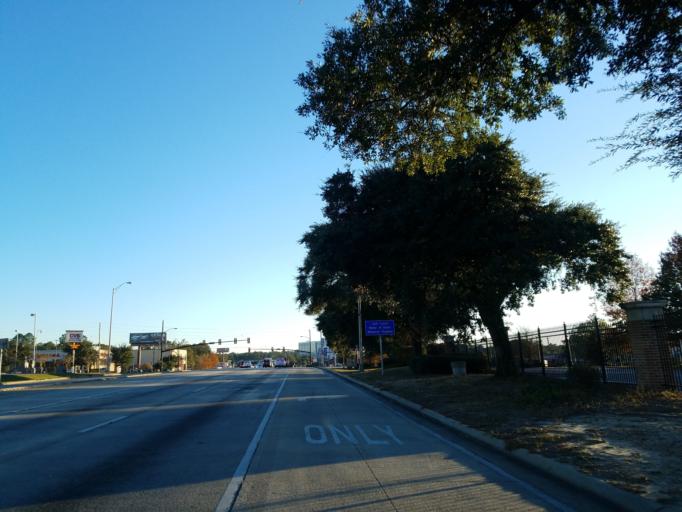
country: US
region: Mississippi
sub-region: Forrest County
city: Hattiesburg
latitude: 31.3261
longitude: -89.3291
